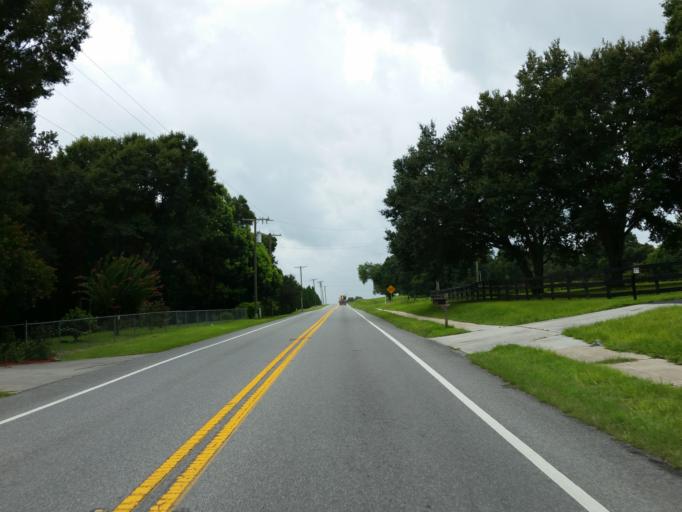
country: US
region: Florida
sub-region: Hillsborough County
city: Thonotosassa
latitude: 28.0479
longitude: -82.3027
